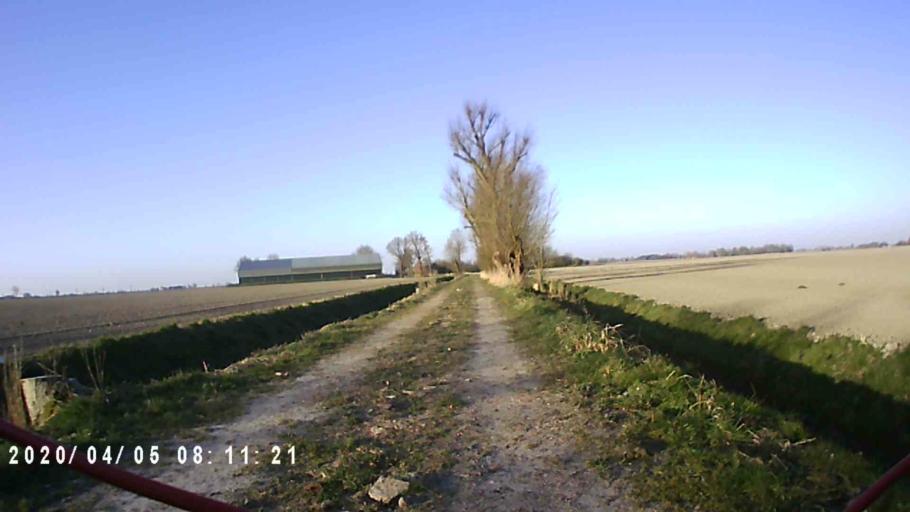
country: NL
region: Groningen
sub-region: Gemeente Zuidhorn
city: Oldehove
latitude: 53.3480
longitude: 6.4461
